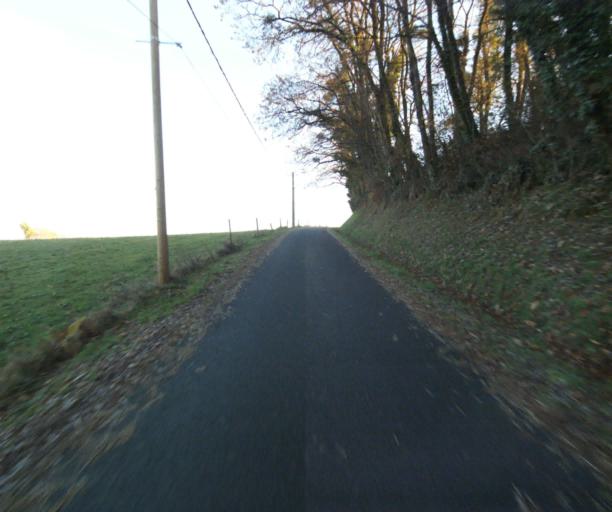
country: FR
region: Limousin
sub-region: Departement de la Correze
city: Laguenne
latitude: 45.2318
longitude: 1.8251
